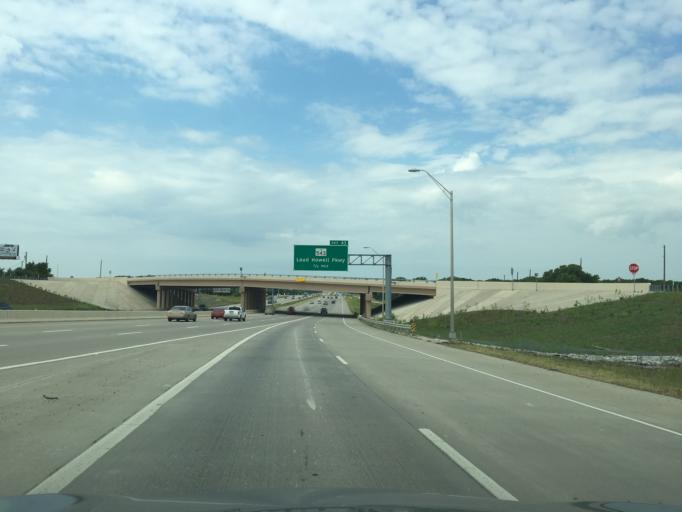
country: US
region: Texas
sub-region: Collin County
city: Melissa
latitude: 33.2615
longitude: -96.6042
